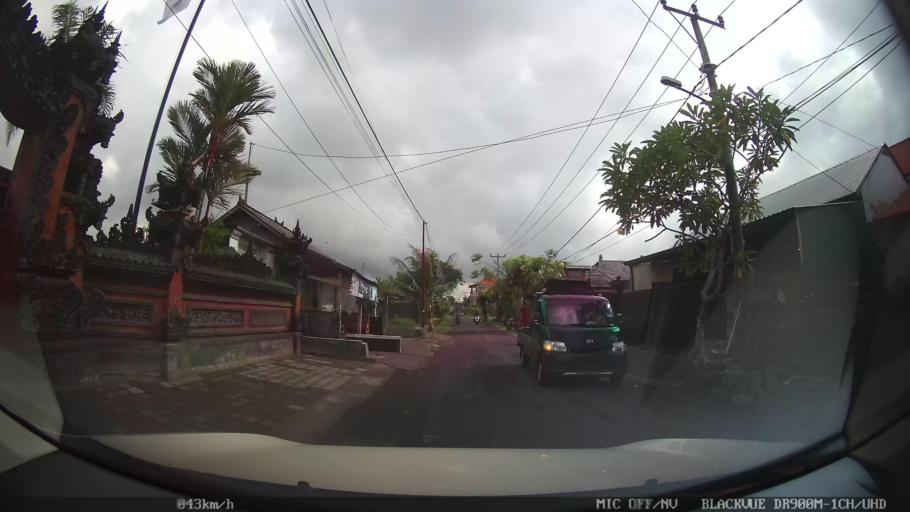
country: ID
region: Bali
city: Banjar Bucu
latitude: -8.5940
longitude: 115.2063
